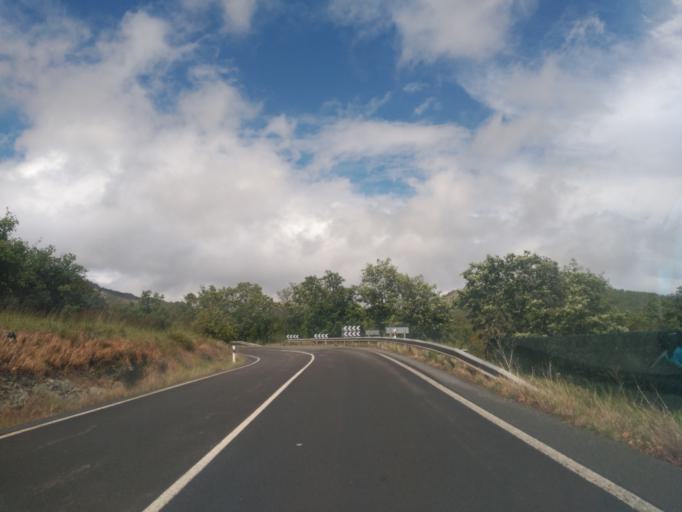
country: ES
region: Castille and Leon
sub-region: Provincia de Salamanca
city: Vallejera de Riofrio
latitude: 40.4002
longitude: -5.7289
